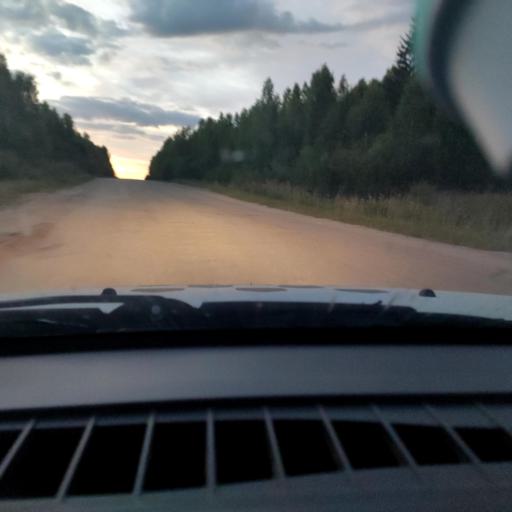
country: RU
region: Kirov
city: Darovskoy
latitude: 59.0125
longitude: 47.8750
